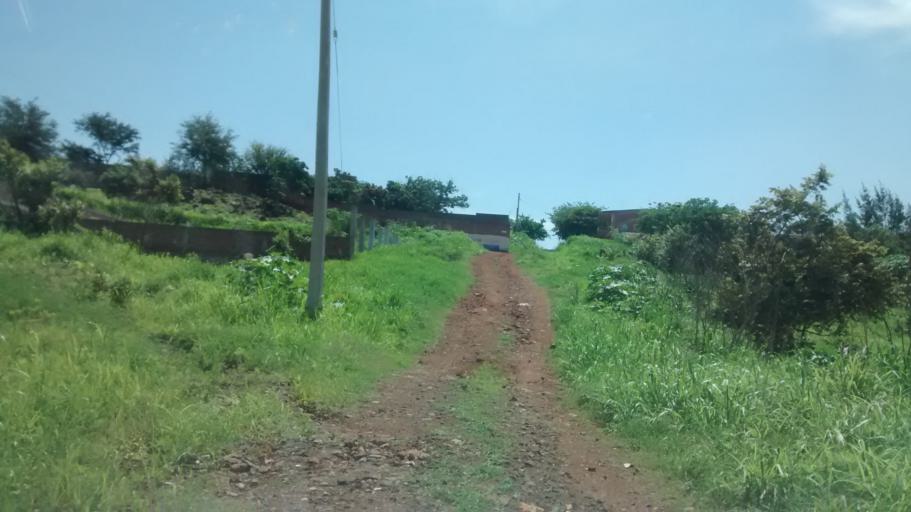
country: MX
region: Nayarit
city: Ixtlan del Rio
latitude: 21.0284
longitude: -104.3556
